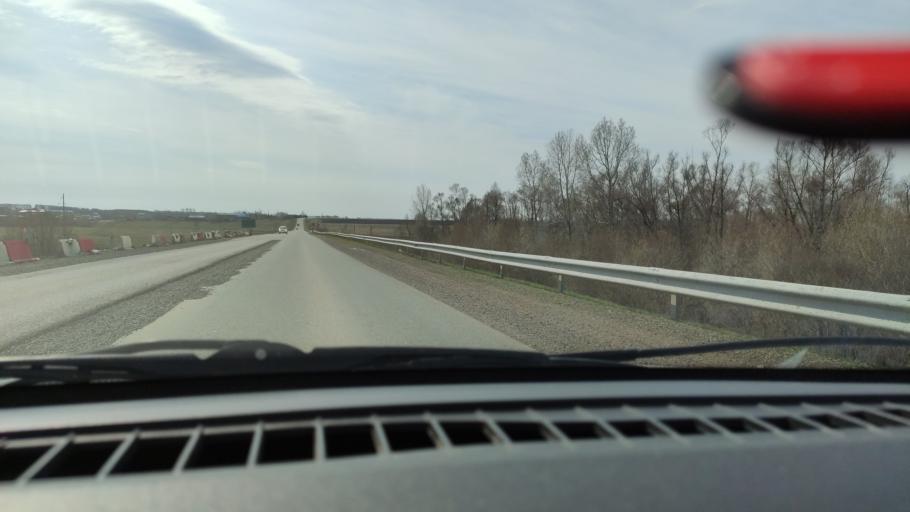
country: RU
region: Bashkortostan
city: Dyurtyuli
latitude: 55.5098
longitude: 54.8347
